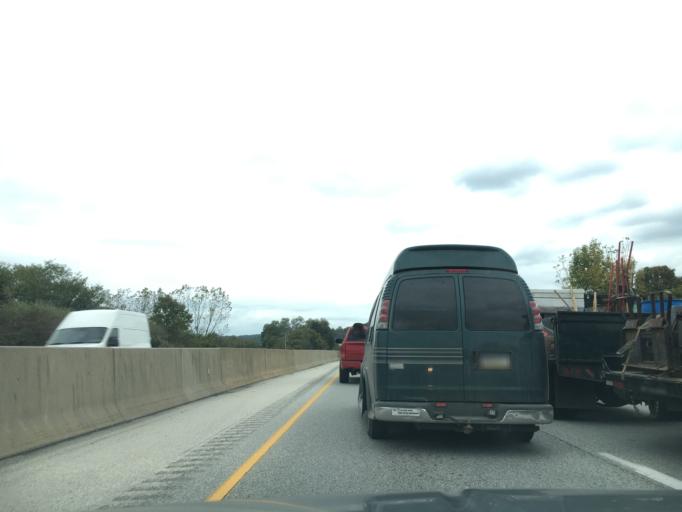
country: US
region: Pennsylvania
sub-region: Chester County
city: Downingtown
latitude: 40.0189
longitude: -75.6738
